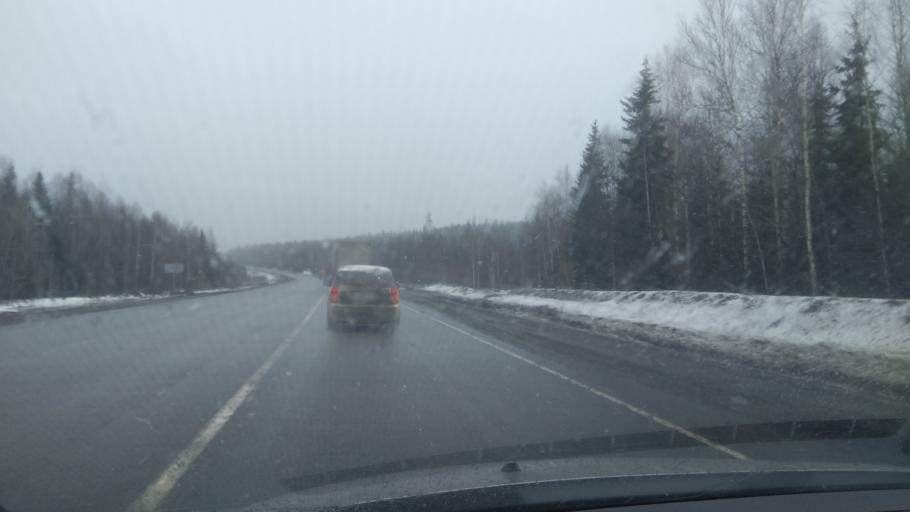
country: RU
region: Sverdlovsk
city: Arti
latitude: 56.7887
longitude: 58.5715
